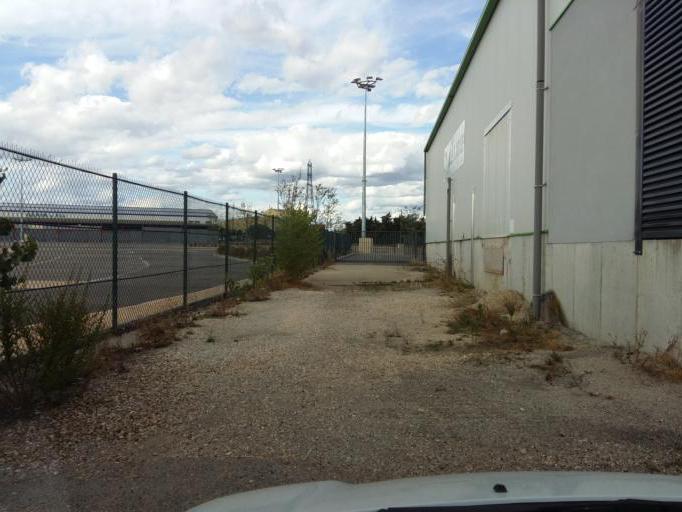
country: FR
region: Provence-Alpes-Cote d'Azur
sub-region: Departement du Vaucluse
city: Carpentras
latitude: 44.0330
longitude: 5.0439
